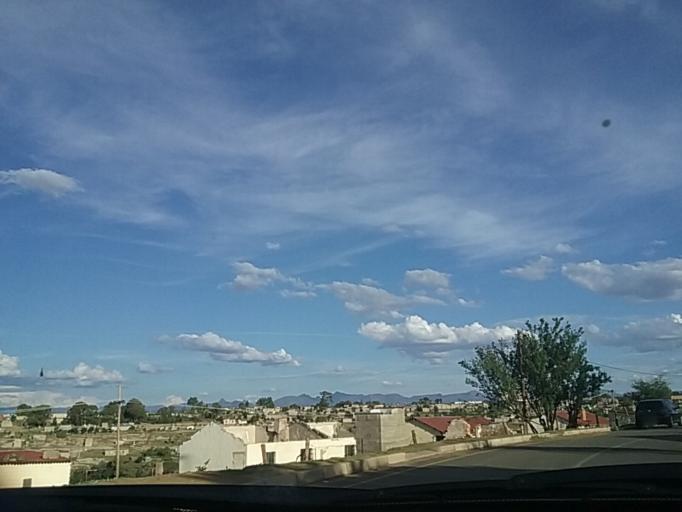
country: LS
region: Berea
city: Teyateyaneng
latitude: -29.1432
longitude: 27.7417
